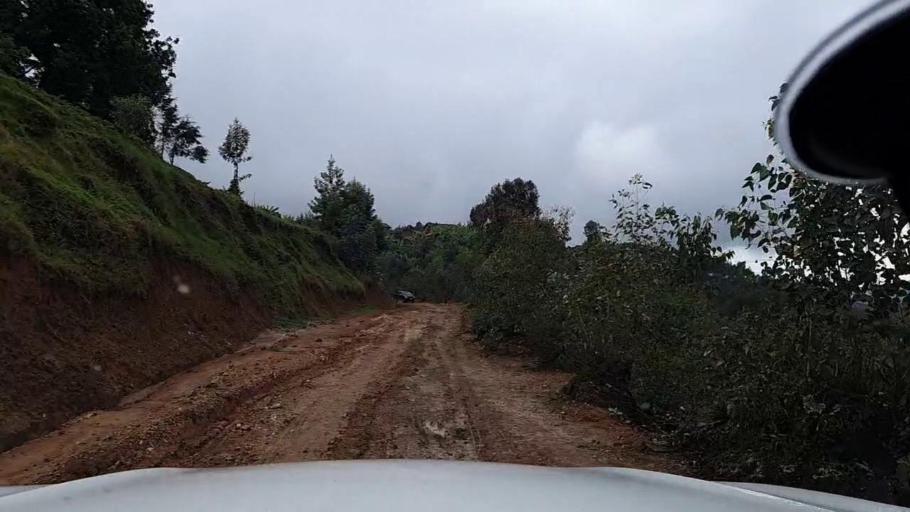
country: RW
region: Western Province
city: Kibuye
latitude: -2.0836
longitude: 29.5104
